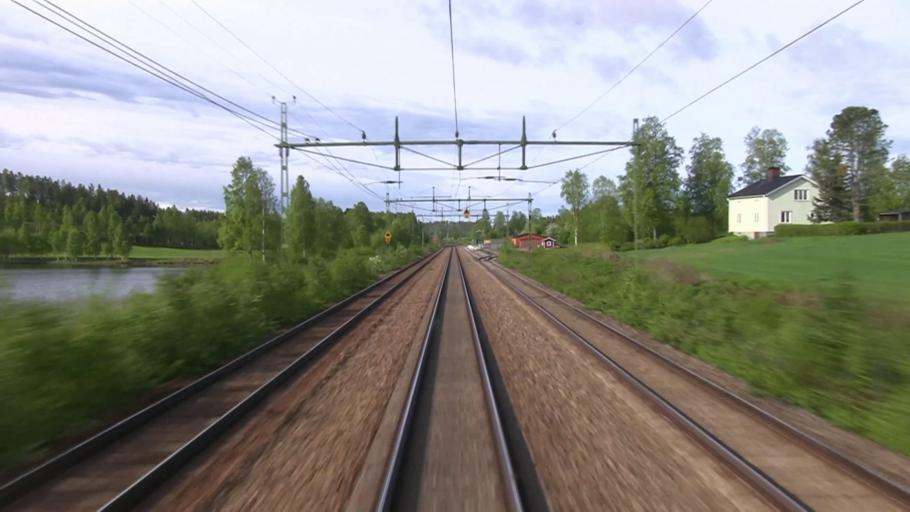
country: SE
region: Vaesterbotten
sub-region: Vindelns Kommun
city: Vindeln
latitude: 64.0999
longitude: 19.6779
